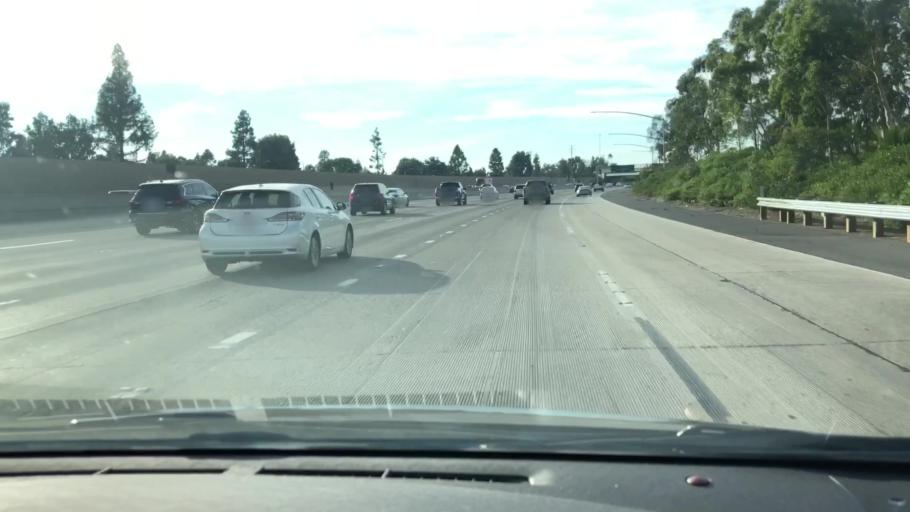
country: US
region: California
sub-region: Orange County
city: Placentia
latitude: 33.8466
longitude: -117.8661
